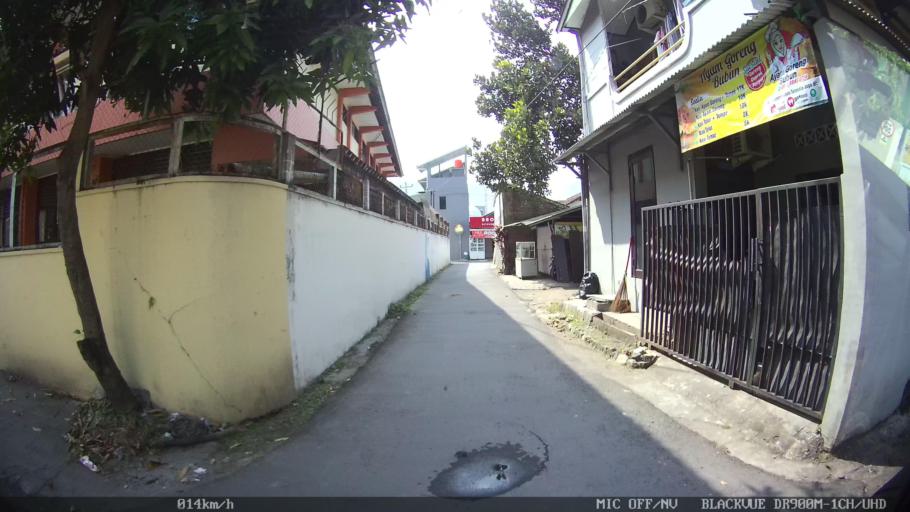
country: ID
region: Daerah Istimewa Yogyakarta
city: Yogyakarta
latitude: -7.8084
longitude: 110.3801
